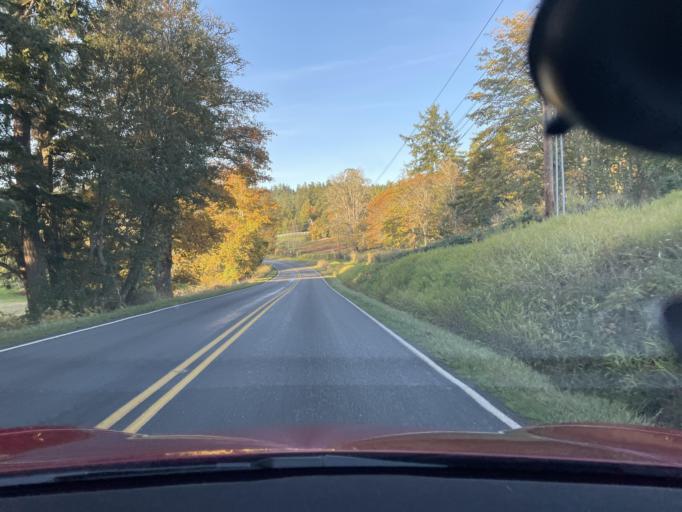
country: US
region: Washington
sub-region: San Juan County
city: Friday Harbor
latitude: 48.5695
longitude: -123.1398
